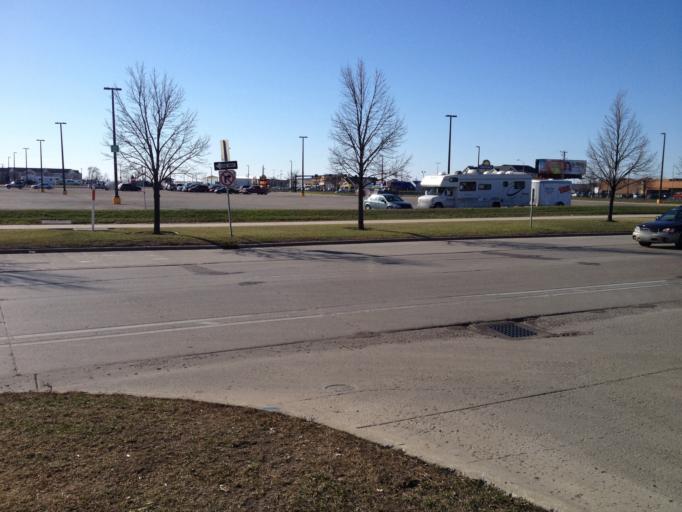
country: US
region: North Dakota
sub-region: Cass County
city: Fargo
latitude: 46.9039
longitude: -96.7979
